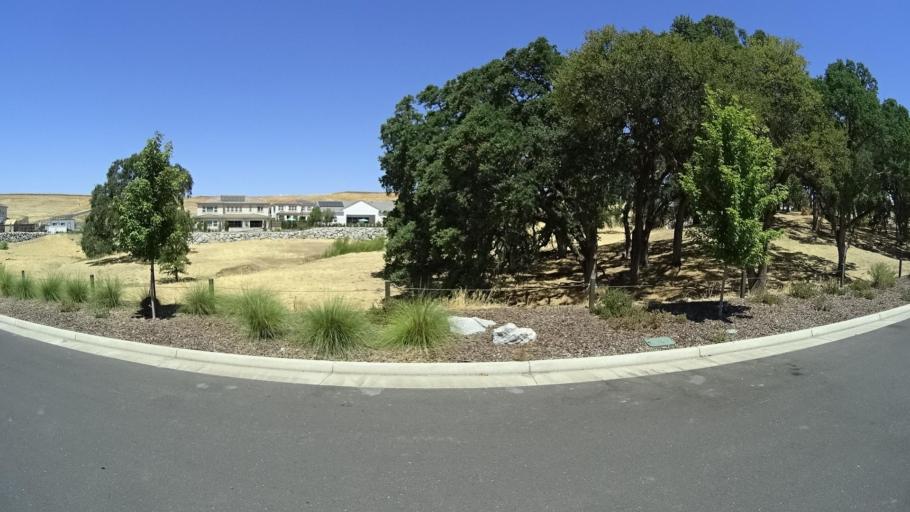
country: US
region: California
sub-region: Placer County
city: Rocklin
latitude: 38.8341
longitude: -121.2526
